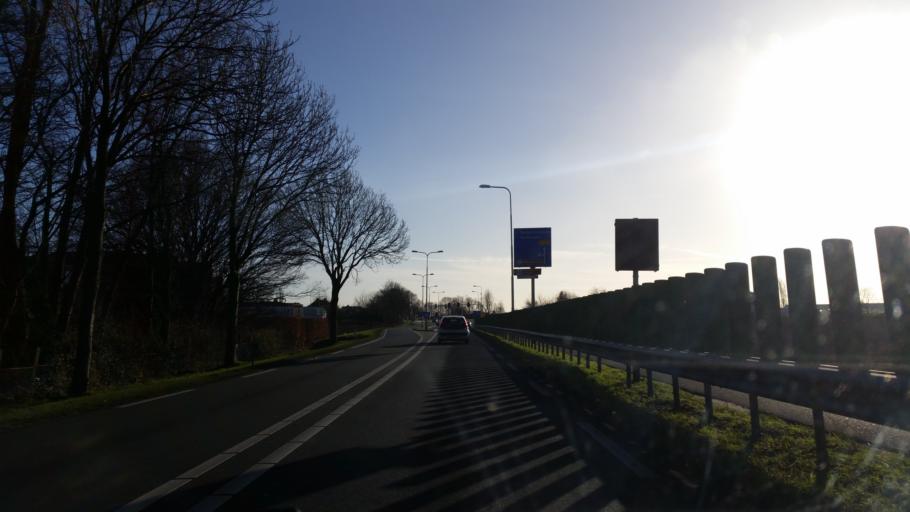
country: NL
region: South Holland
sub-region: Gemeente Lansingerland
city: Bleiswijk
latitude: 52.0067
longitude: 4.5252
